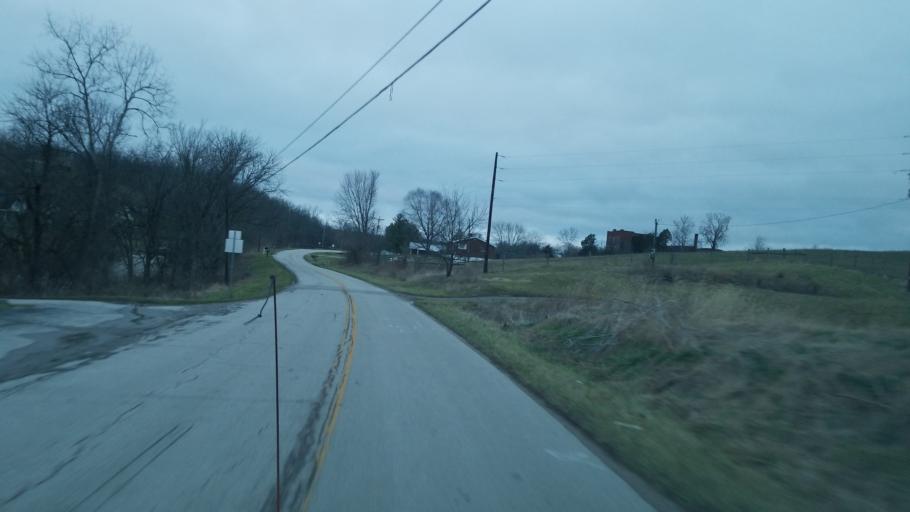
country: US
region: Kentucky
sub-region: Mason County
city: Maysville
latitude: 38.5686
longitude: -83.6903
